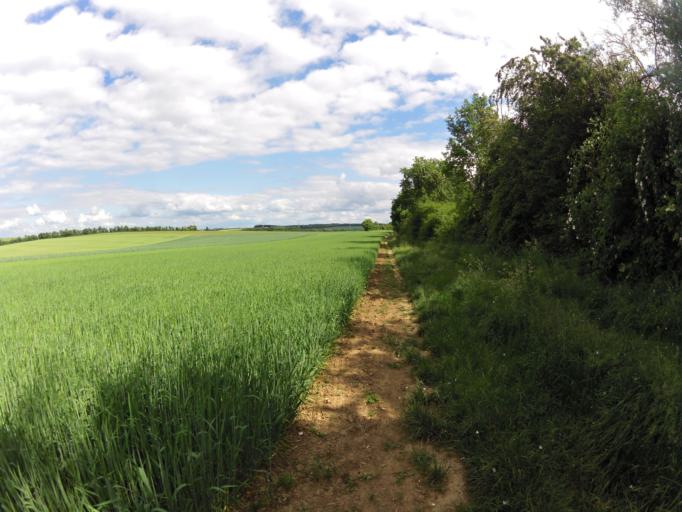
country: DE
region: Bavaria
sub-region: Regierungsbezirk Unterfranken
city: Gaukonigshofen
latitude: 49.6622
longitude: 10.0152
